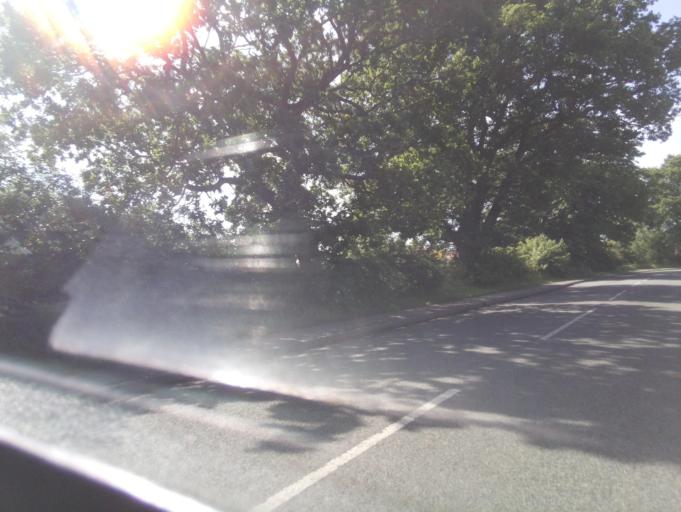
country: GB
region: England
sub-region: Lincolnshire
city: Skellingthorpe
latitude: 53.1342
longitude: -0.6338
